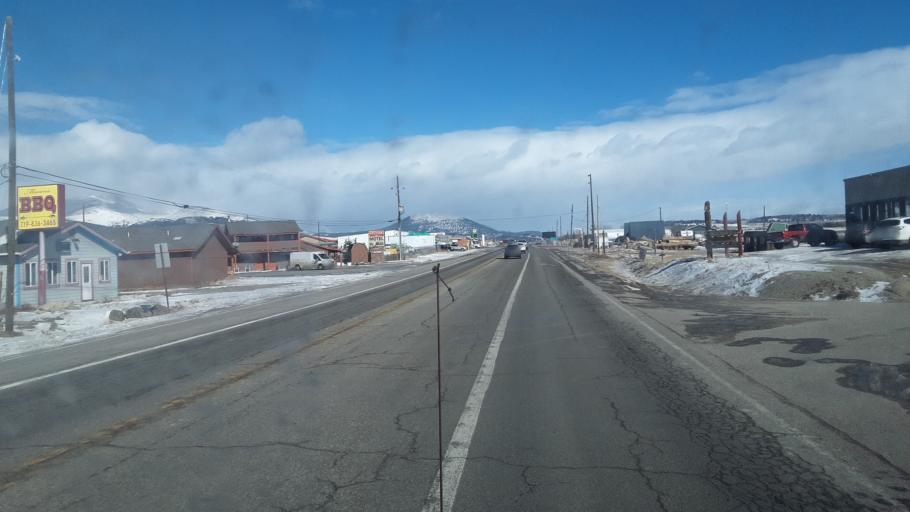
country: US
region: Colorado
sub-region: Park County
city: Fairplay
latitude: 39.2231
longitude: -105.9925
